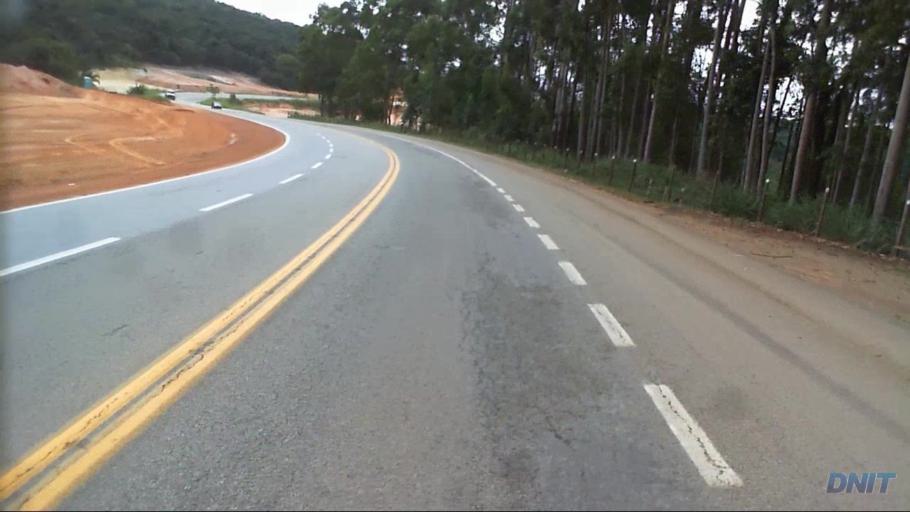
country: BR
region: Minas Gerais
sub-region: Caete
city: Caete
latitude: -19.7477
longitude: -43.5449
